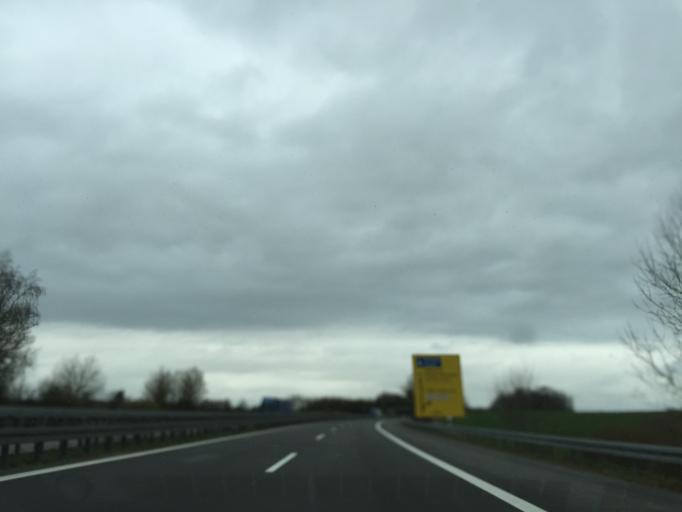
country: DE
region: Baden-Wuerttemberg
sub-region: Freiburg Region
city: Donaueschingen
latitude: 47.9664
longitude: 8.5125
